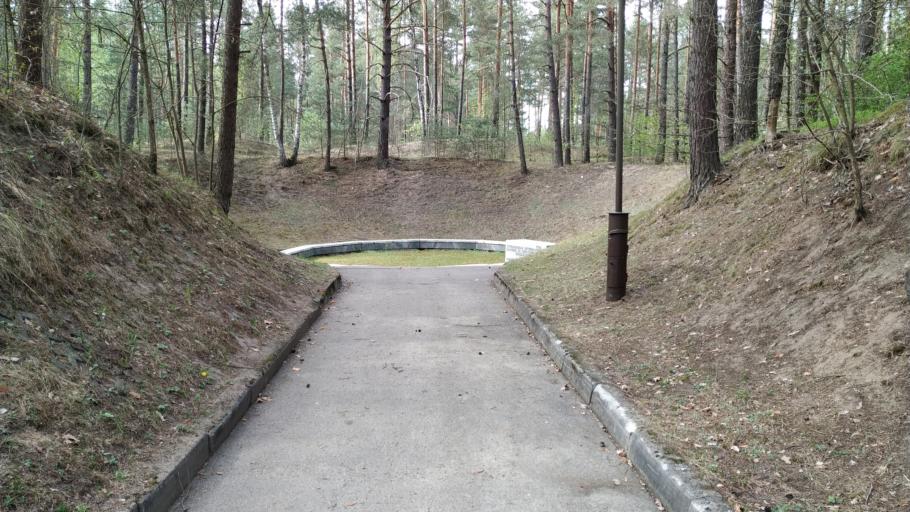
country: LT
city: Baltoji Voke
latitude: 54.6262
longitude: 25.1605
